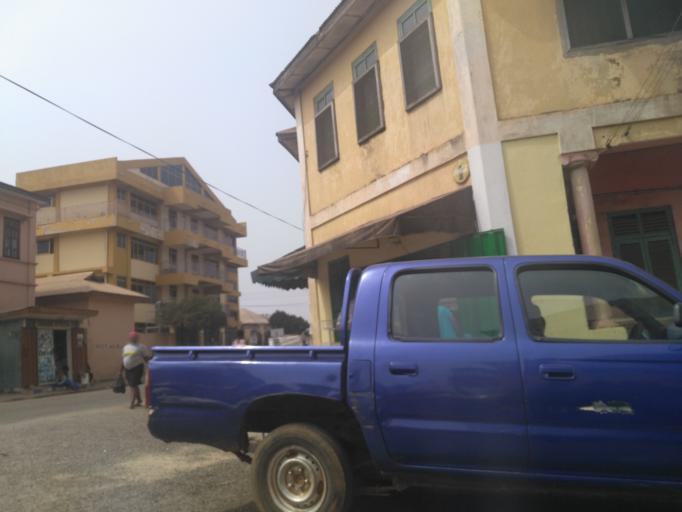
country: GH
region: Ashanti
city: Kumasi
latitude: 6.7068
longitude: -1.6207
